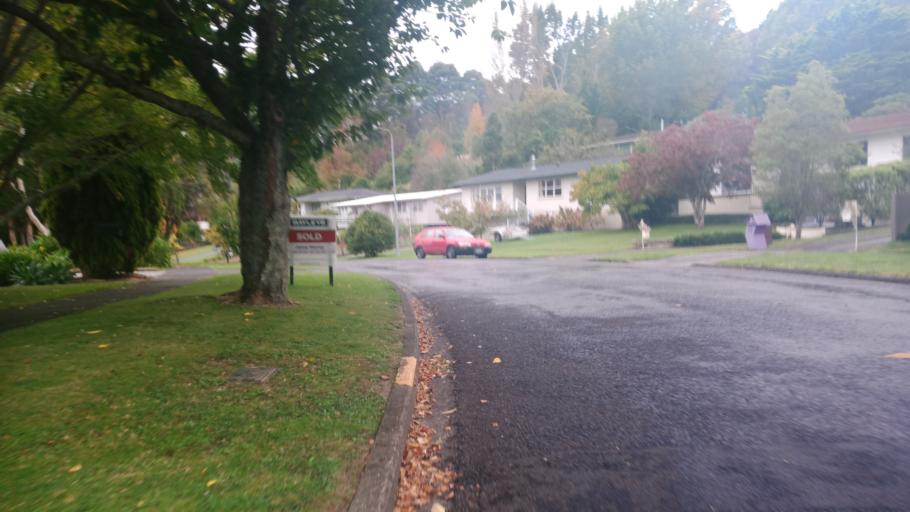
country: NZ
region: Gisborne
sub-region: Gisborne District
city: Gisborne
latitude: -38.6582
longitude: 178.0413
